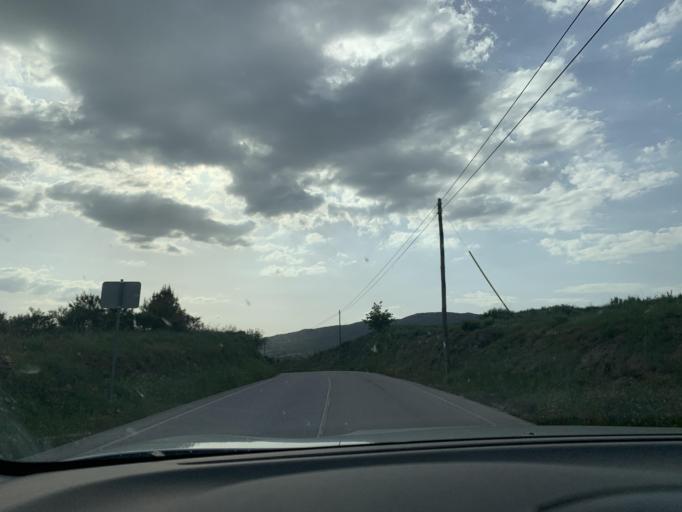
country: PT
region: Guarda
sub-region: Fornos de Algodres
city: Fornos de Algodres
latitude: 40.5816
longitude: -7.6211
